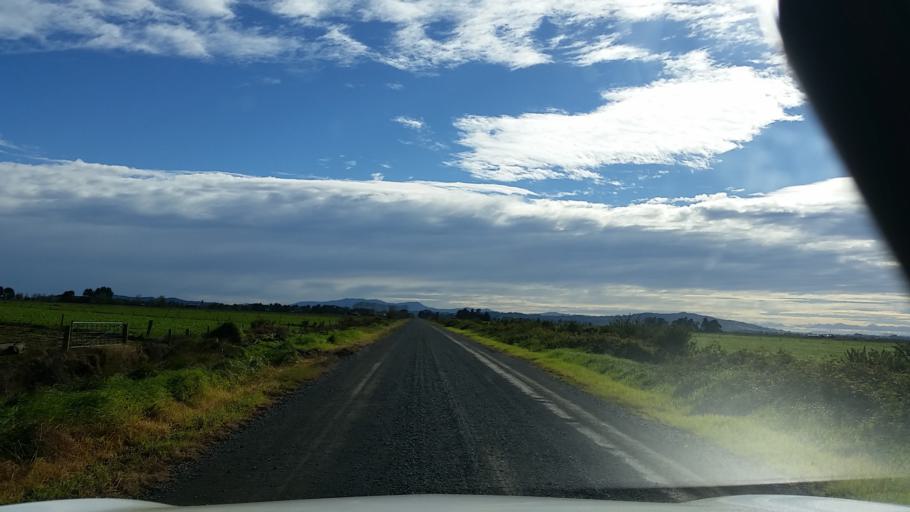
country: NZ
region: Waikato
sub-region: Hamilton City
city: Hamilton
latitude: -37.6802
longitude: 175.4433
